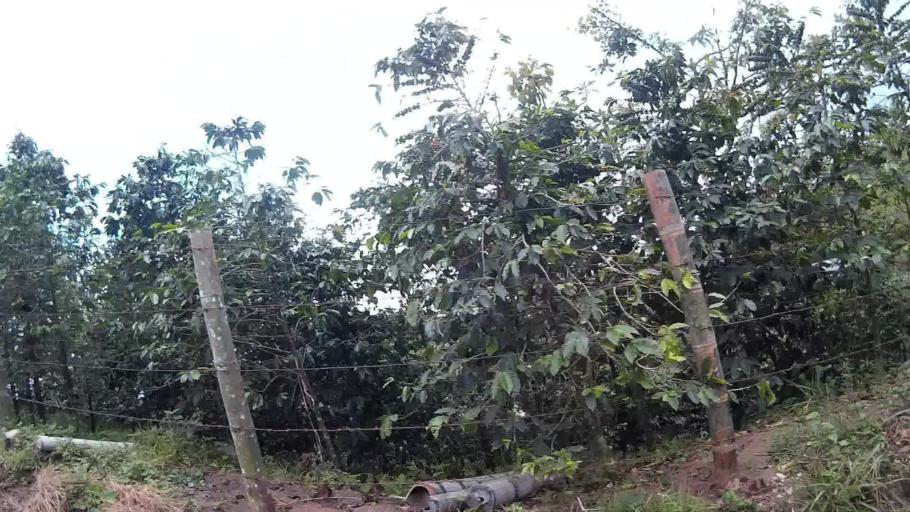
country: CO
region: Valle del Cauca
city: Ulloa
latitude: 4.7237
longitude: -75.6939
